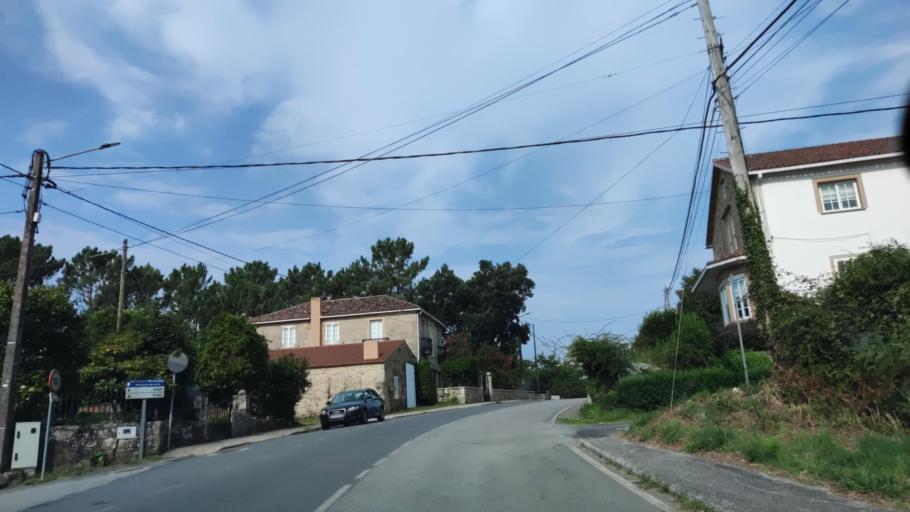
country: ES
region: Galicia
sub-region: Provincia da Coruna
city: Rianxo
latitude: 42.6465
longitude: -8.7864
